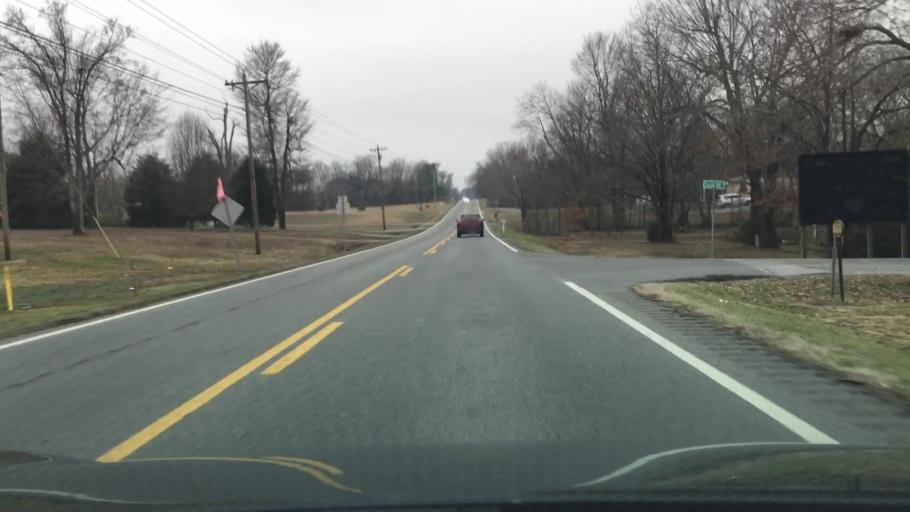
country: US
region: Kentucky
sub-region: Marshall County
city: Calvert City
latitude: 36.9730
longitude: -88.4036
